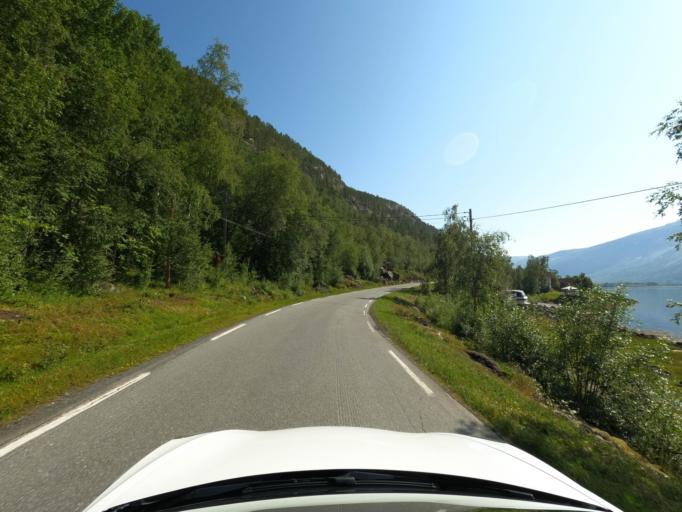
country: NO
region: Nordland
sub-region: Narvik
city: Narvik
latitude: 68.2744
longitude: 17.3983
